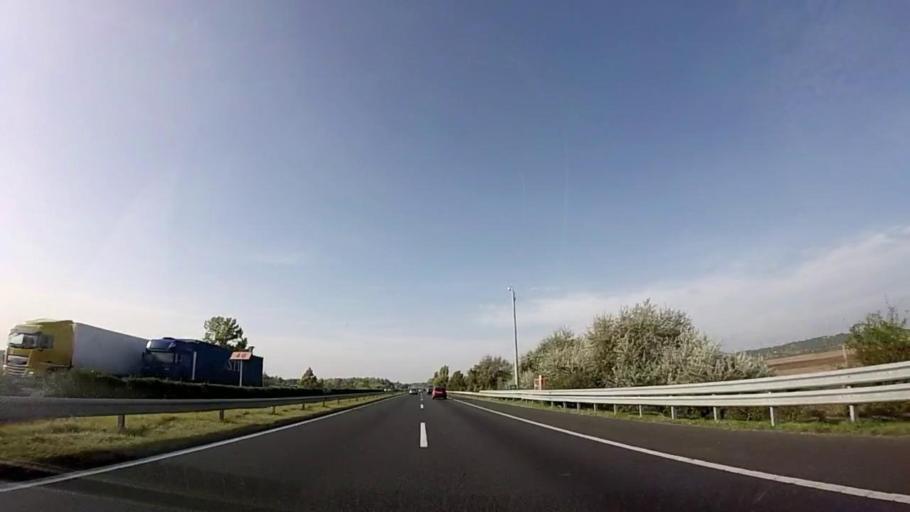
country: HU
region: Fejer
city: Kapolnasnyek
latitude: 47.2670
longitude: 18.6878
